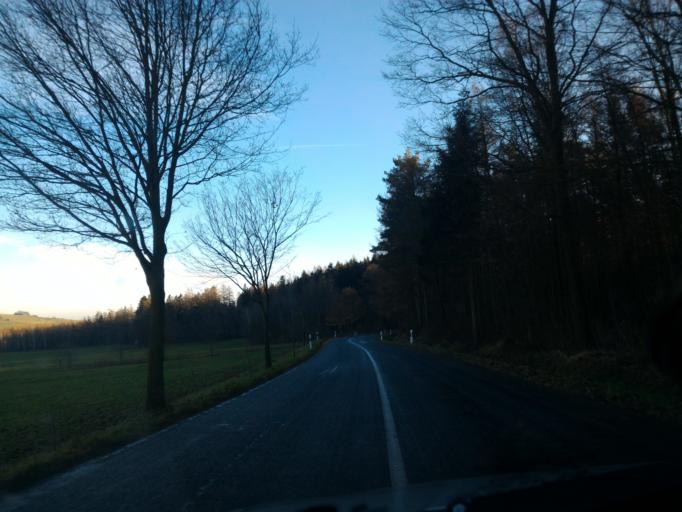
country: DE
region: Saxony
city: Grossschonau
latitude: 50.8653
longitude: 14.6719
